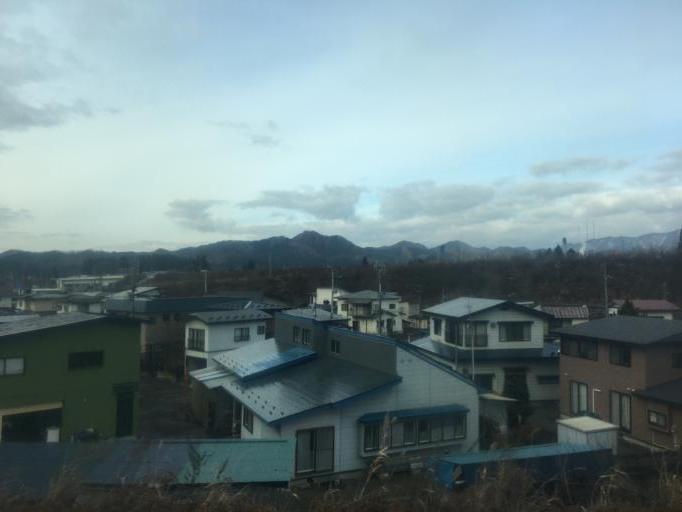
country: JP
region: Akita
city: Odate
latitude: 40.3037
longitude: 140.5692
